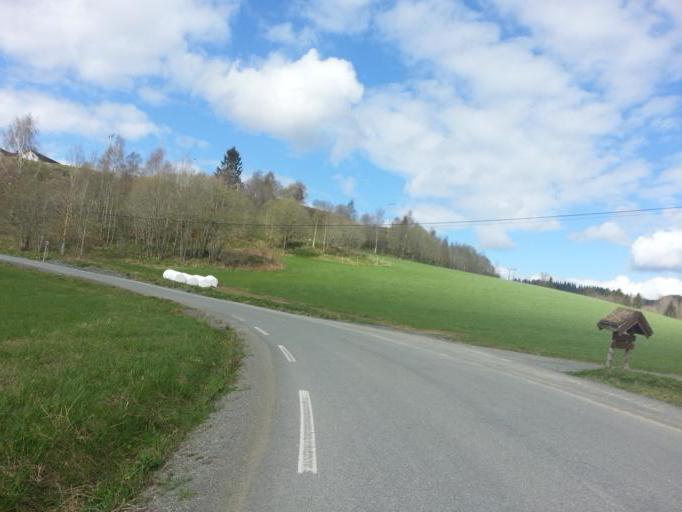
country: NO
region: Nord-Trondelag
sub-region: Levanger
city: Skogn
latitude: 63.6339
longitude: 11.2775
